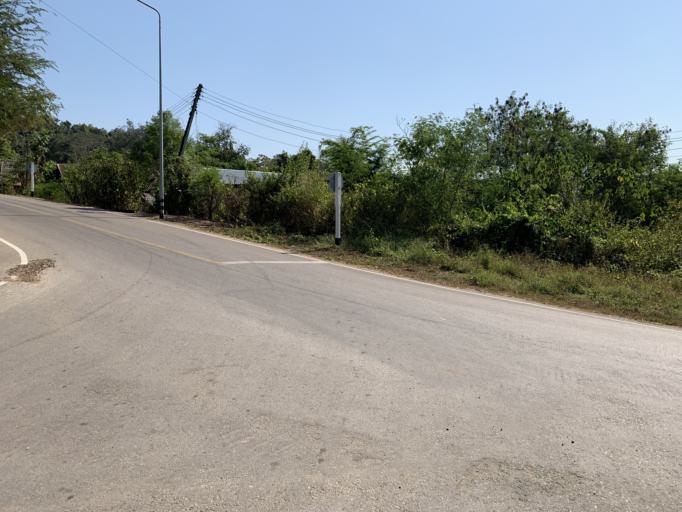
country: TH
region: Tak
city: Phop Phra
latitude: 16.4835
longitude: 98.6449
